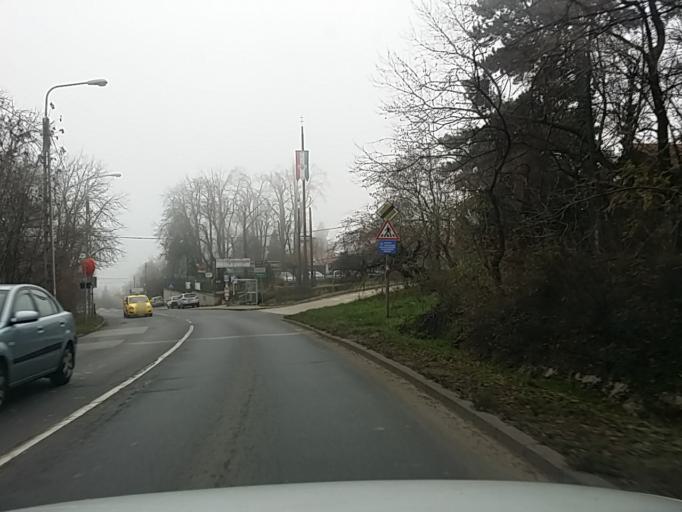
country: HU
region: Pest
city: Budakeszi
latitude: 47.5211
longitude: 18.9391
